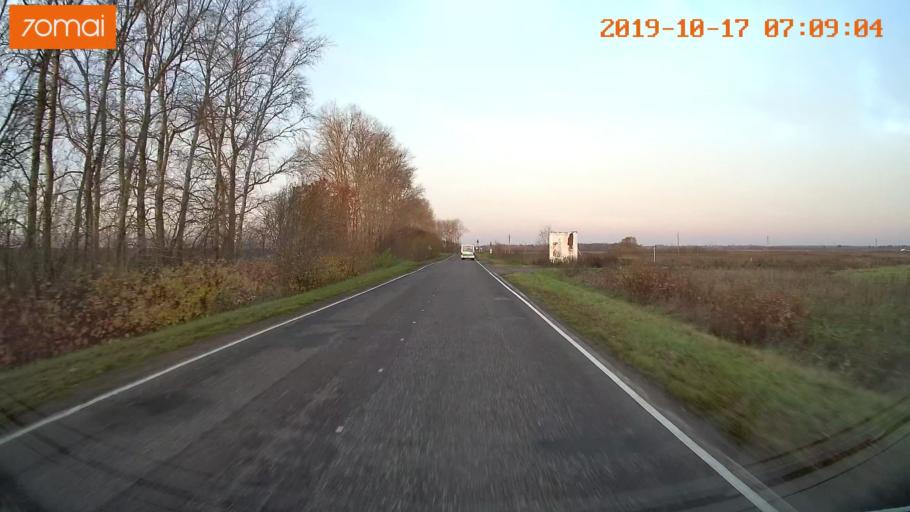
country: RU
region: Vladimir
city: Suzdal'
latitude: 56.4205
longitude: 40.3912
